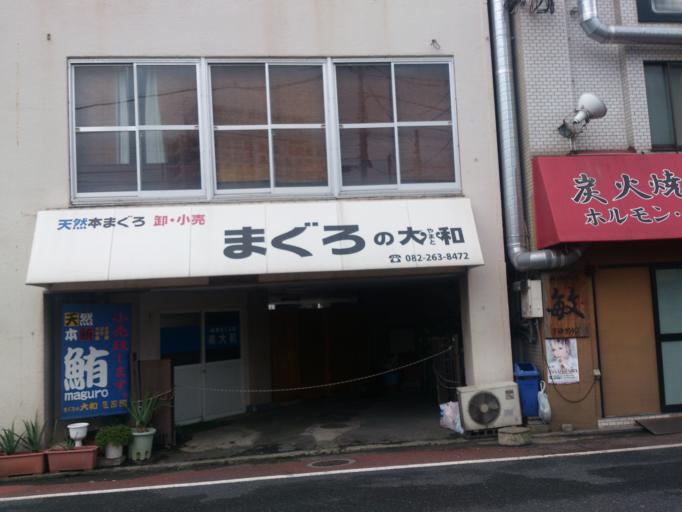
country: JP
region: Hiroshima
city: Hiroshima-shi
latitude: 34.3954
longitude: 132.4788
